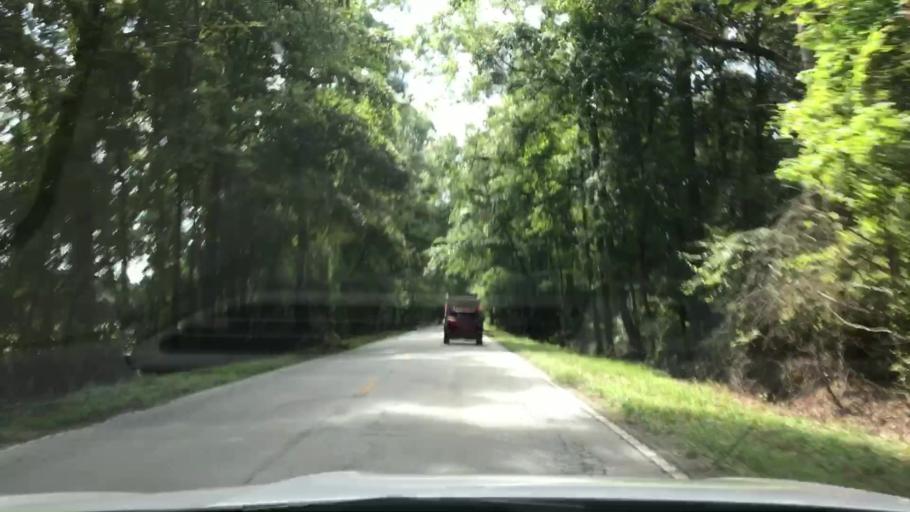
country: US
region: South Carolina
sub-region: Berkeley County
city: Ladson
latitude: 32.8932
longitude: -80.1323
